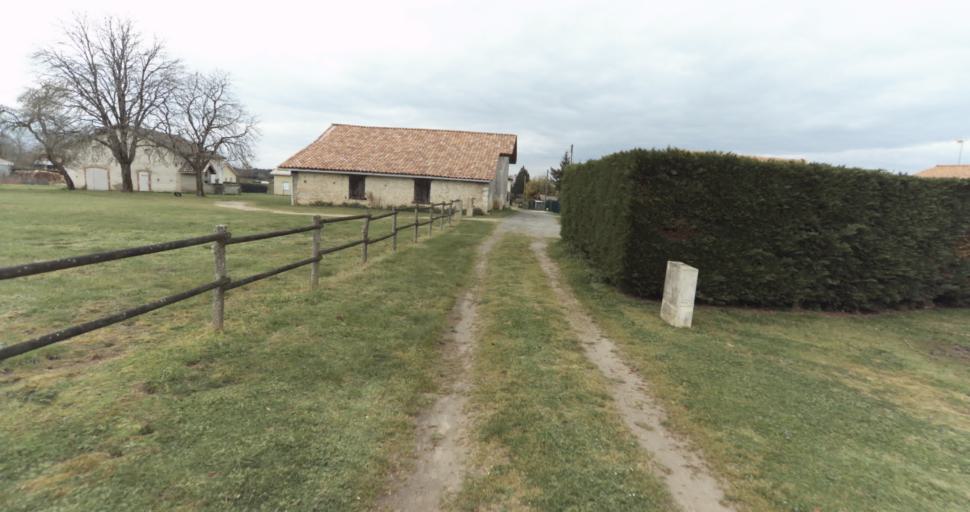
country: FR
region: Aquitaine
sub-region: Departement des Landes
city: Roquefort
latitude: 44.0238
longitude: -0.3338
